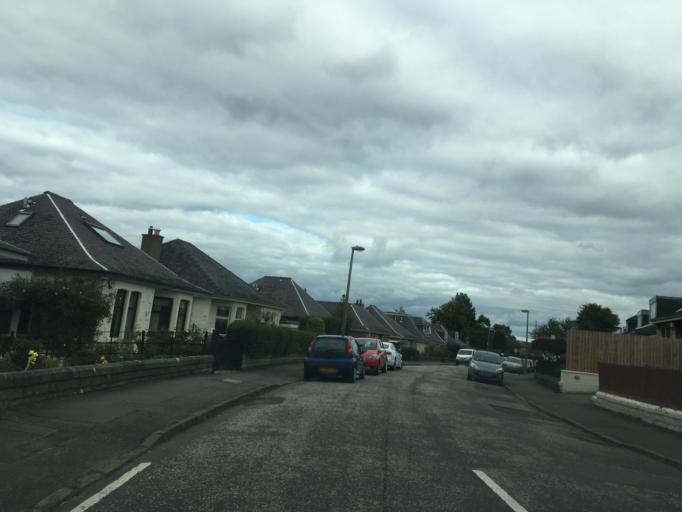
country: GB
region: Scotland
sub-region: Edinburgh
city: Colinton
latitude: 55.9224
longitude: -3.2464
